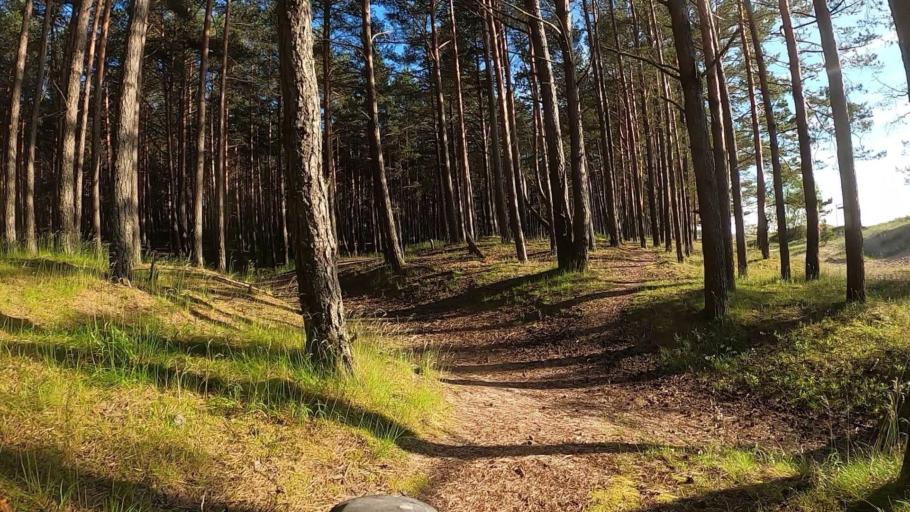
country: LV
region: Riga
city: Jaunciems
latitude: 57.1139
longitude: 24.1915
